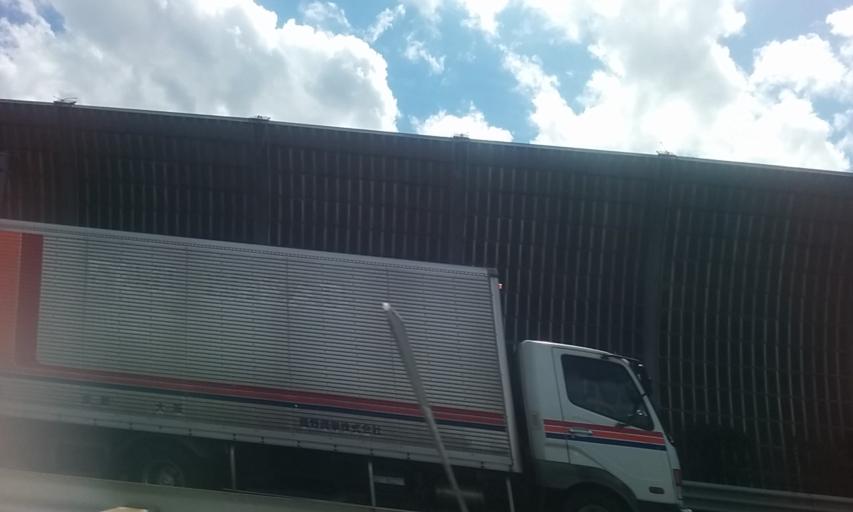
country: JP
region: Shiga Prefecture
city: Otsu-shi
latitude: 34.9537
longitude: 135.9033
